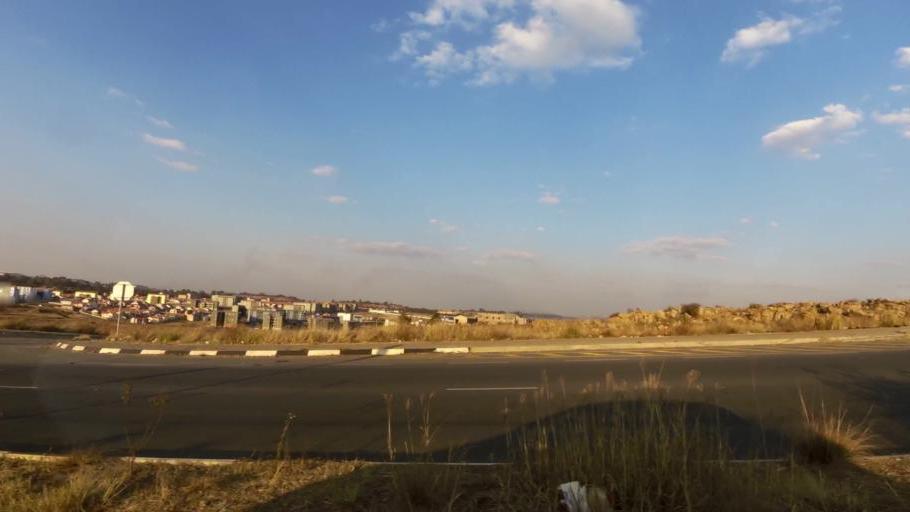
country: ZA
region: Gauteng
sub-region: City of Johannesburg Metropolitan Municipality
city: Roodepoort
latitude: -26.2068
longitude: 27.9044
